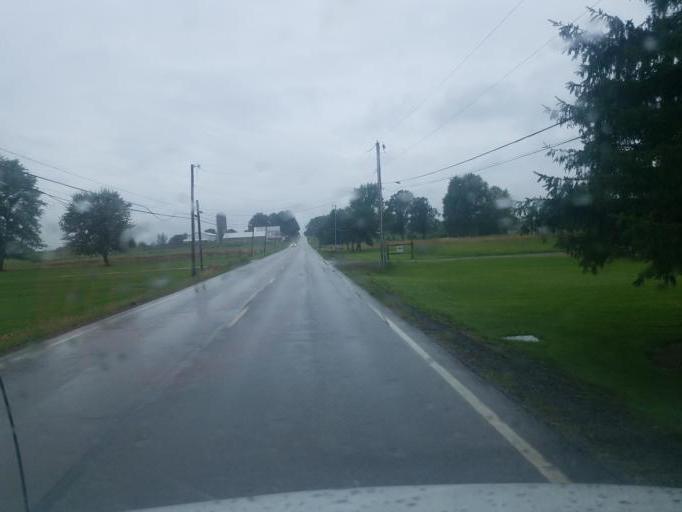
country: US
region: Ohio
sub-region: Medina County
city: Seville
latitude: 41.0251
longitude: -81.8193
